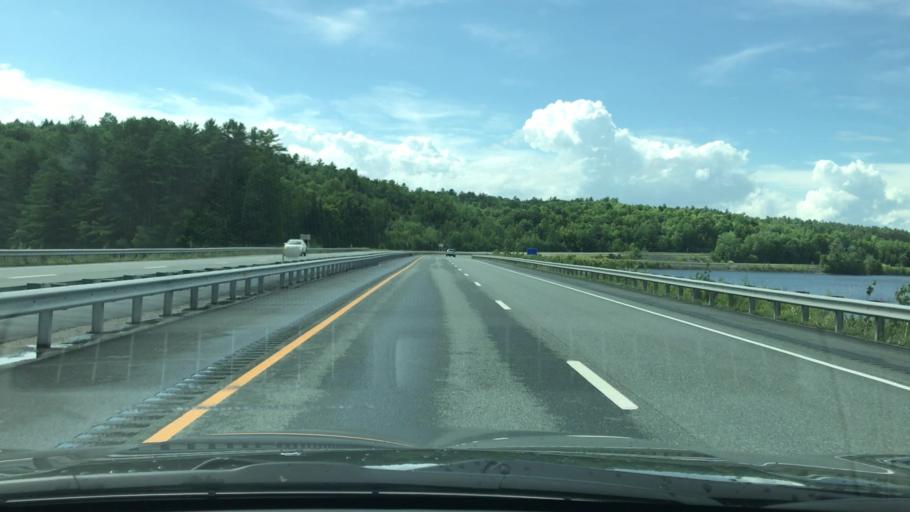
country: US
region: New Hampshire
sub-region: Grafton County
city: Littleton
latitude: 44.3160
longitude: -71.8607
